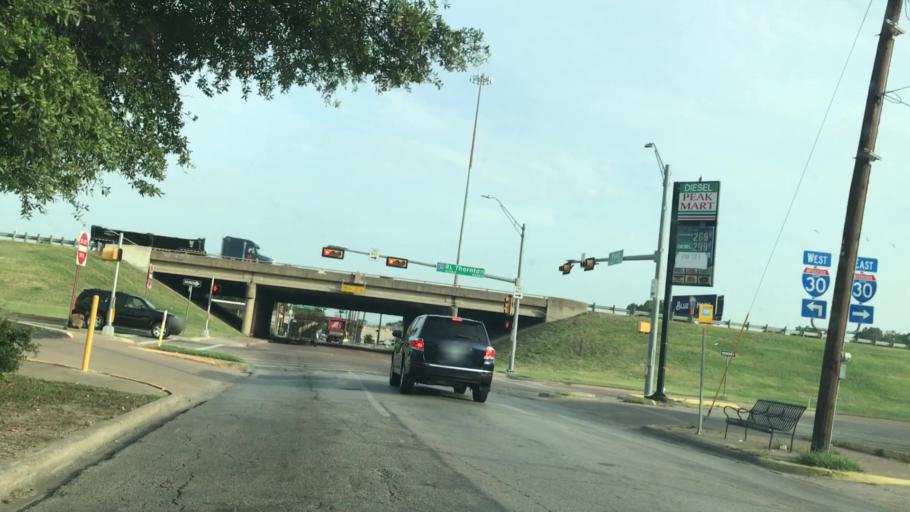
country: US
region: Texas
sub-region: Dallas County
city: Dallas
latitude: 32.7867
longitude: -96.7652
